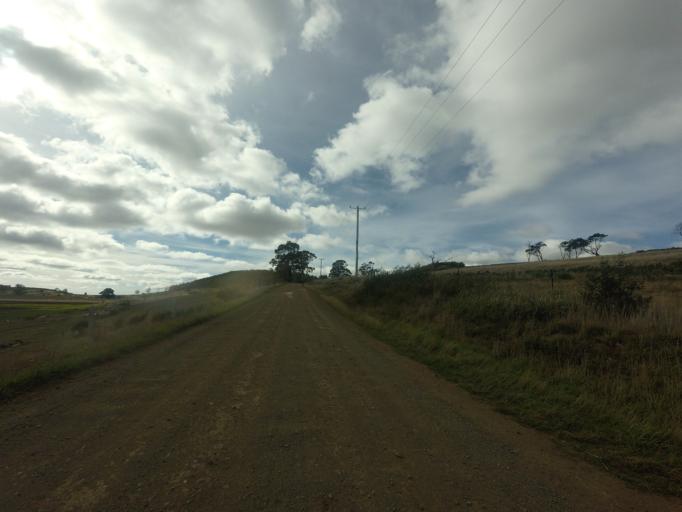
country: AU
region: Tasmania
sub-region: Brighton
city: Bridgewater
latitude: -42.3896
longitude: 147.3995
